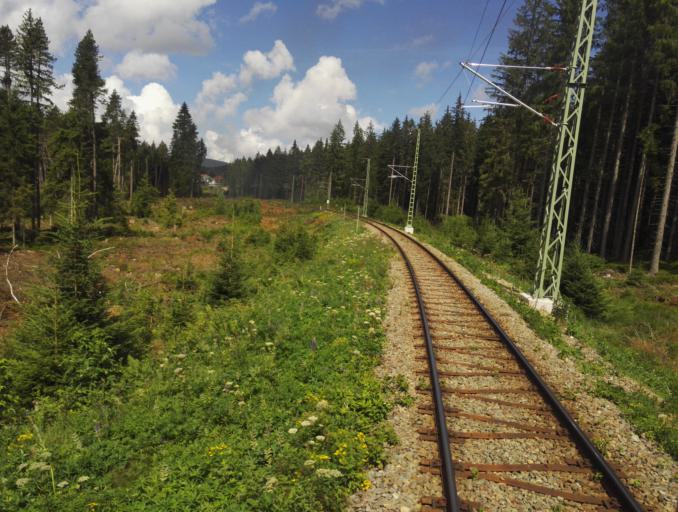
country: DE
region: Baden-Wuerttemberg
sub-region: Freiburg Region
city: Hinterzarten
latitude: 47.8658
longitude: 8.1038
